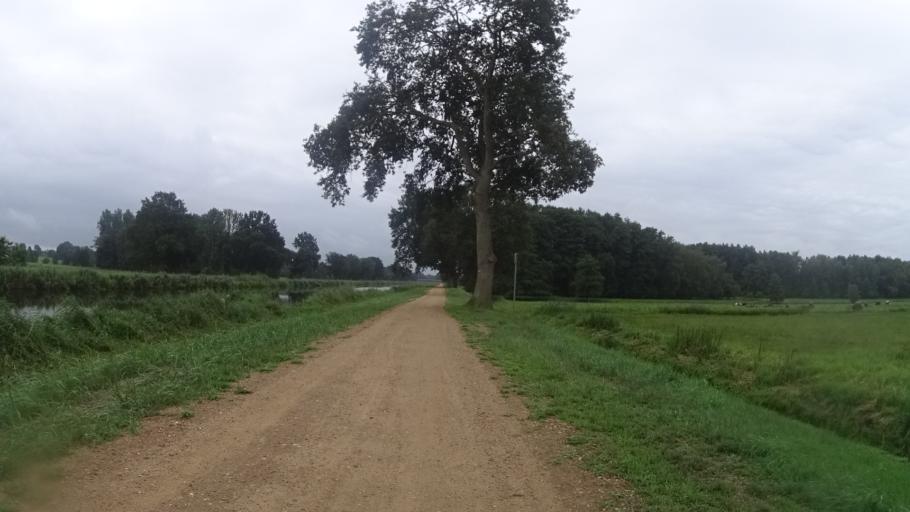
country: DE
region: Schleswig-Holstein
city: Buchen
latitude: 53.4895
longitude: 10.6300
